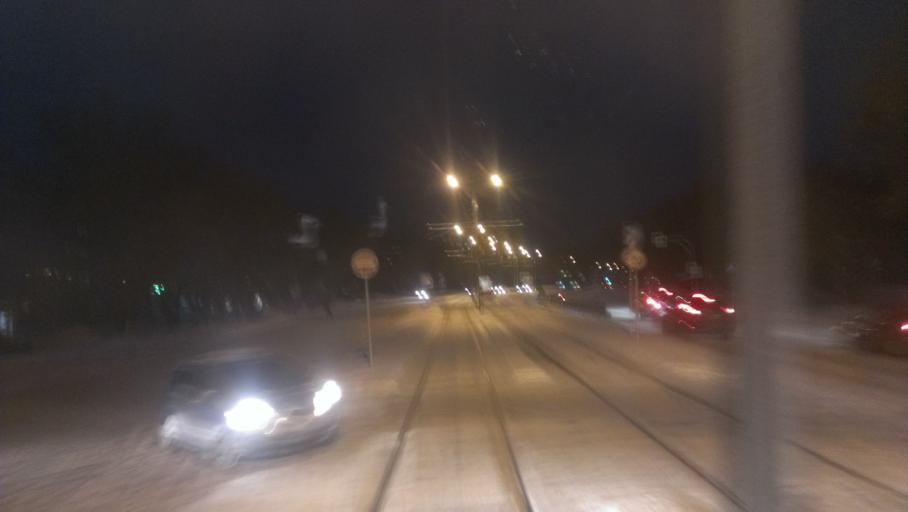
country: RU
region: Altai Krai
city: Novosilikatnyy
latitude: 53.3736
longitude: 83.6782
